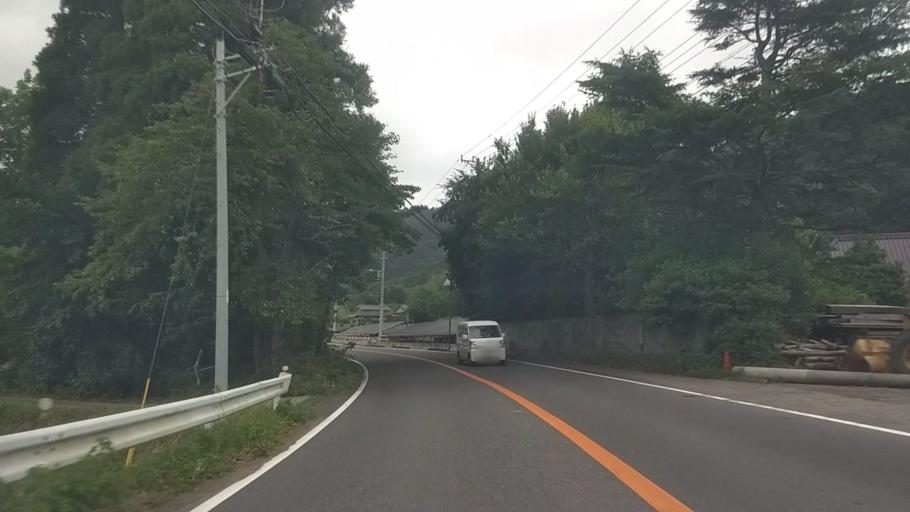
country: JP
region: Chiba
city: Kawaguchi
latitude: 35.1418
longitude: 139.9729
